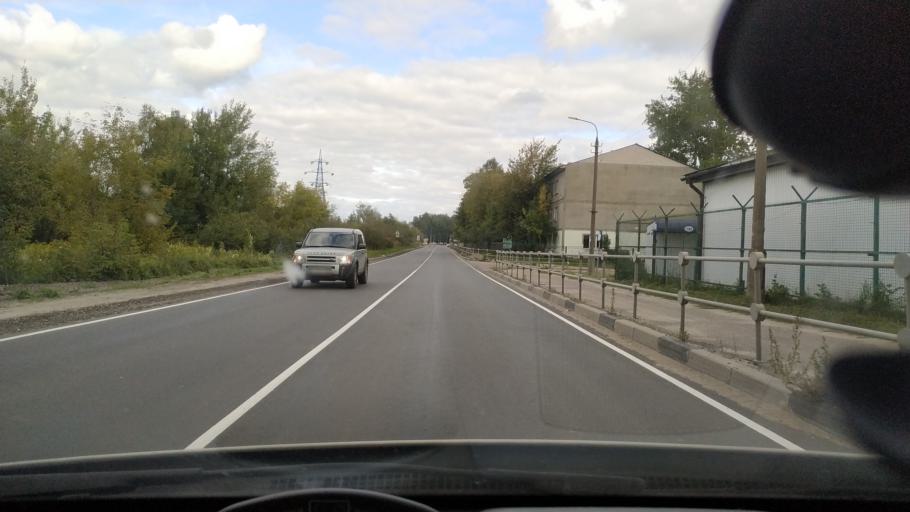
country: RU
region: Moskovskaya
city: Kabanovo
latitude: 55.7381
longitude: 38.9369
